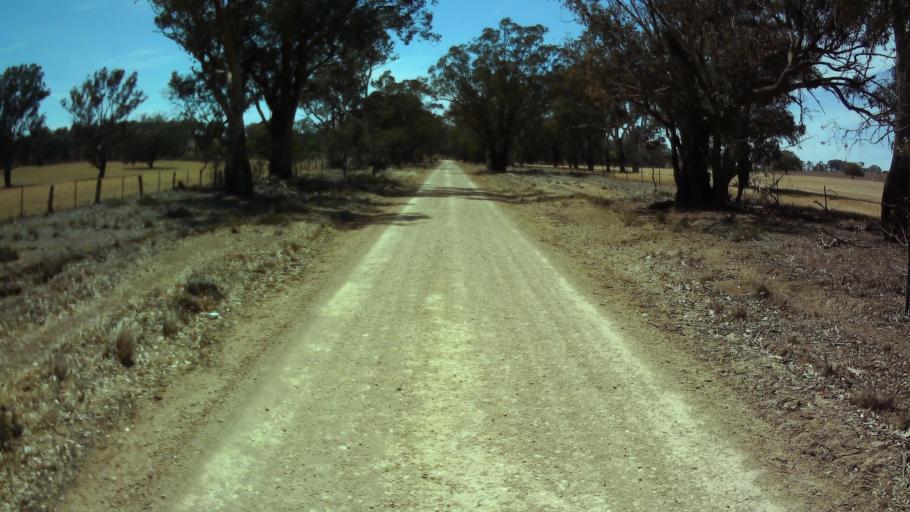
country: AU
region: New South Wales
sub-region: Weddin
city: Grenfell
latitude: -33.9459
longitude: 148.1656
